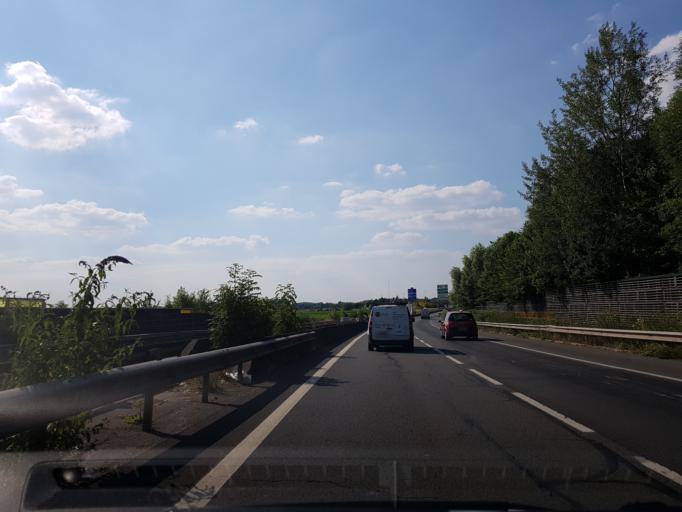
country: FR
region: Nord-Pas-de-Calais
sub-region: Departement du Nord
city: Waziers
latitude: 50.3920
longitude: 3.1226
